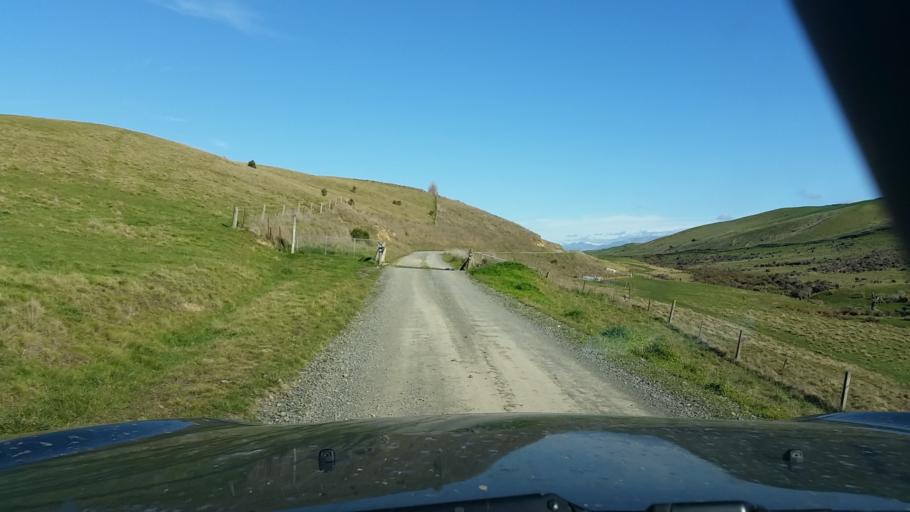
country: NZ
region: Marlborough
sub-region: Marlborough District
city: Blenheim
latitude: -41.6670
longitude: 174.1409
